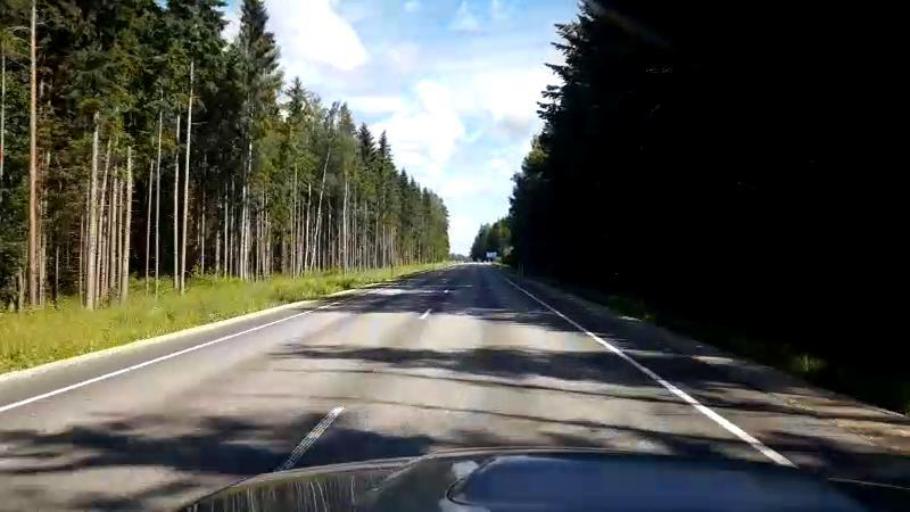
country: EE
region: Jaervamaa
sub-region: Paide linn
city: Paide
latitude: 58.9652
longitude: 25.6603
